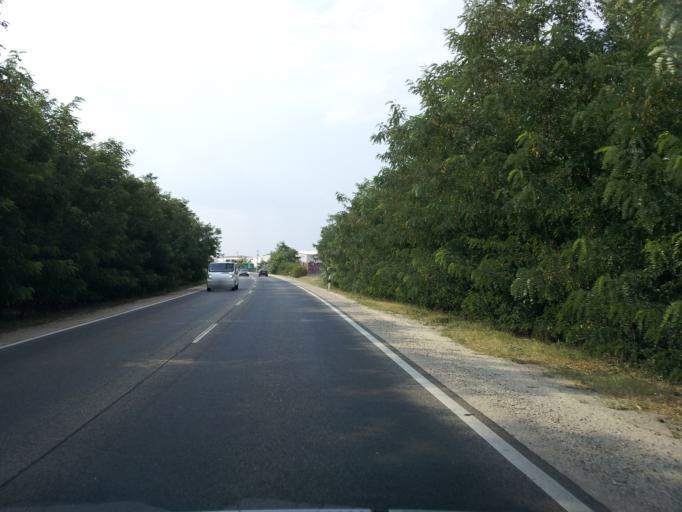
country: HU
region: Pest
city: Dunaharaszti
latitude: 47.3591
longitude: 19.1228
